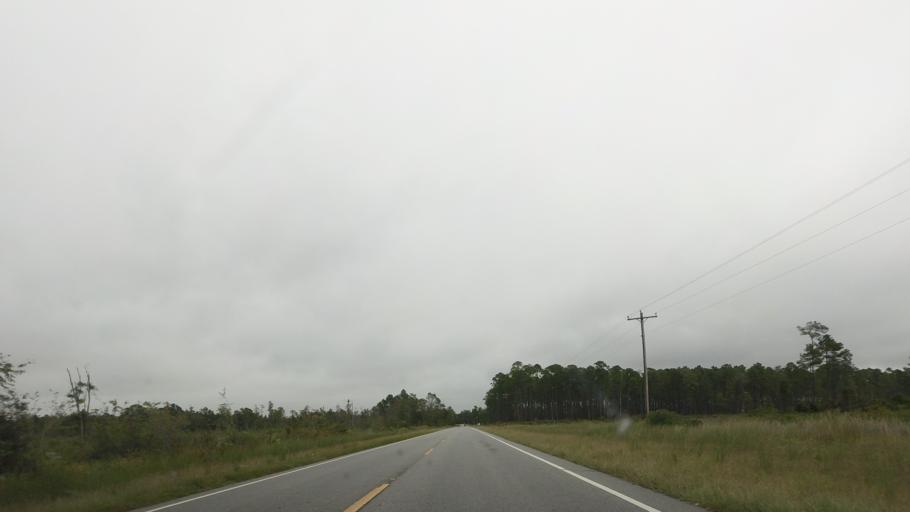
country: US
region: Georgia
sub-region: Berrien County
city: Nashville
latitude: 31.2943
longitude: -83.2360
